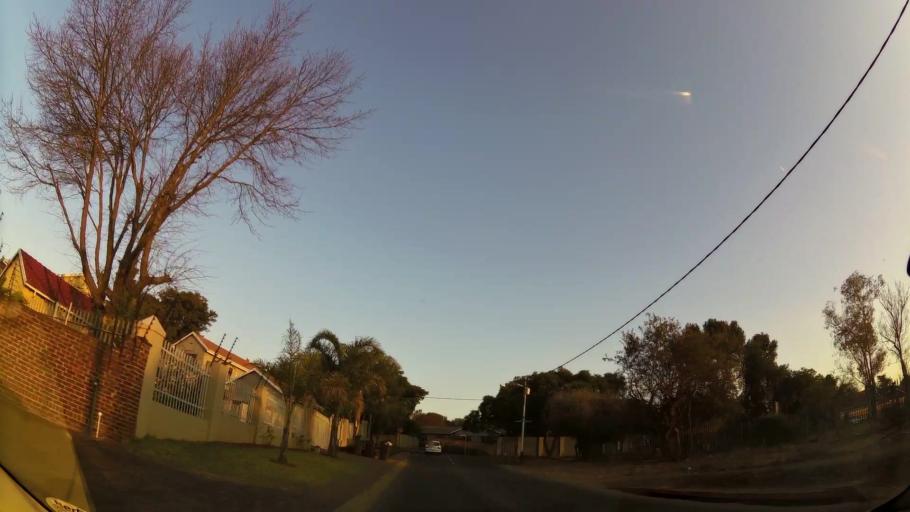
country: ZA
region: Gauteng
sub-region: City of Johannesburg Metropolitan Municipality
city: Johannesburg
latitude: -26.1196
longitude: 27.9948
